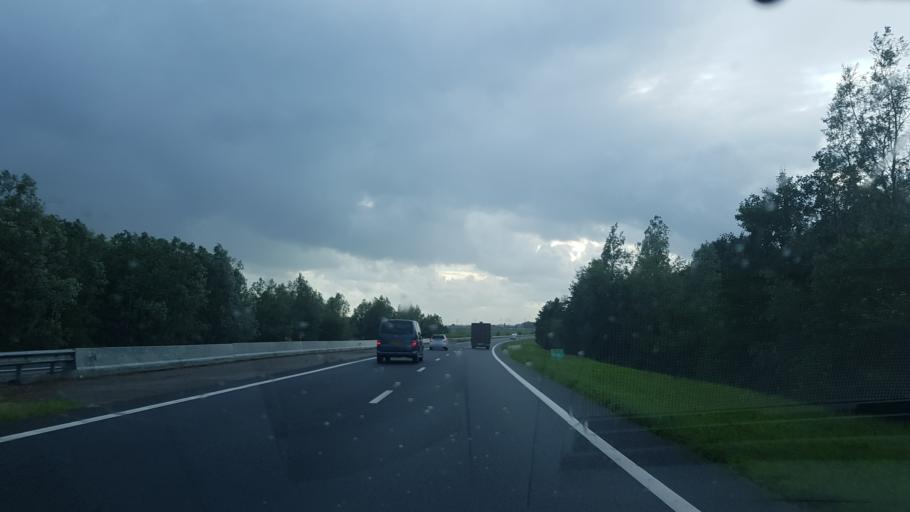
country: NL
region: Friesland
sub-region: Gemeente Boarnsterhim
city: Warten
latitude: 53.1648
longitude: 5.9264
